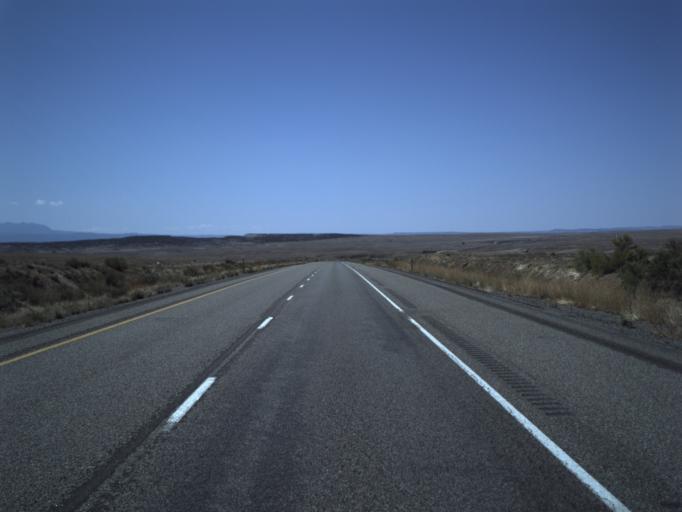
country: US
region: Colorado
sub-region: Mesa County
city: Loma
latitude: 39.1424
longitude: -109.1543
